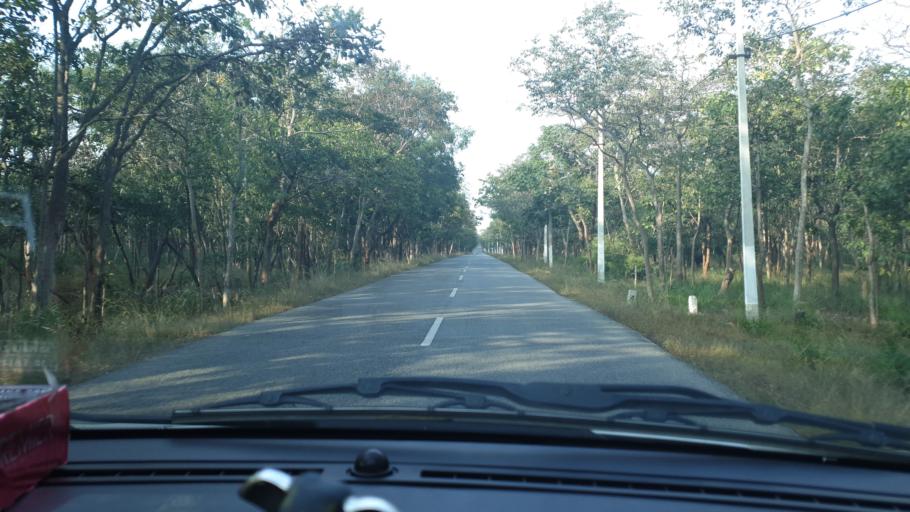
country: IN
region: Andhra Pradesh
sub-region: Kurnool
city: Srisailam
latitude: 16.2936
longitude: 78.7307
